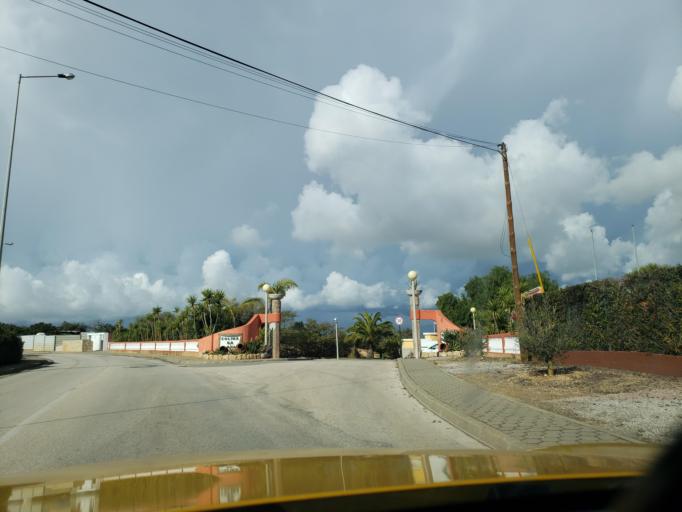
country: PT
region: Faro
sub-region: Lagoa
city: Estombar
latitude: 37.1115
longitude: -8.4927
